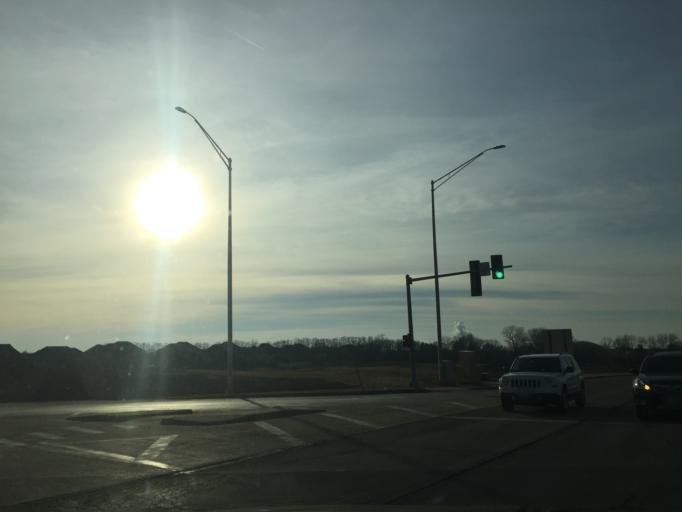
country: US
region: Illinois
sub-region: Cook County
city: Lemont
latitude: 41.6562
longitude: -88.0192
